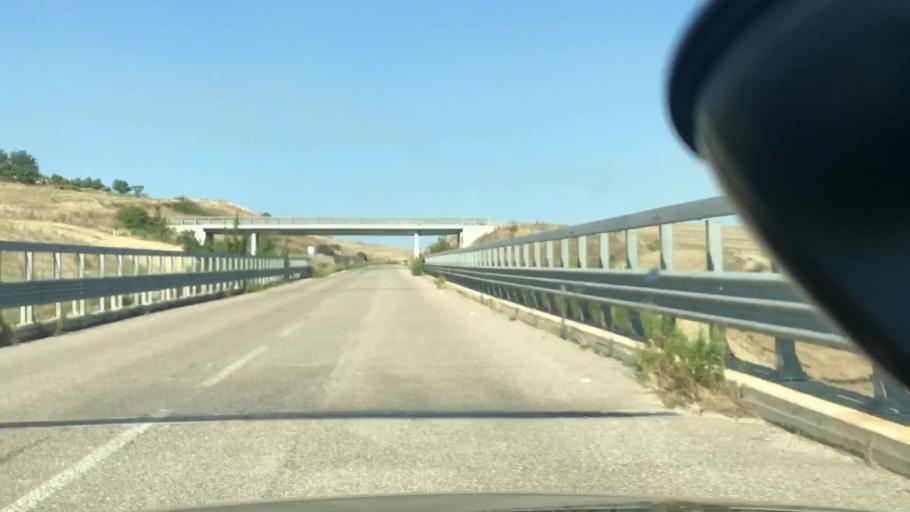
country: IT
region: Basilicate
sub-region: Provincia di Matera
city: Grottole
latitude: 40.6929
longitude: 16.4335
